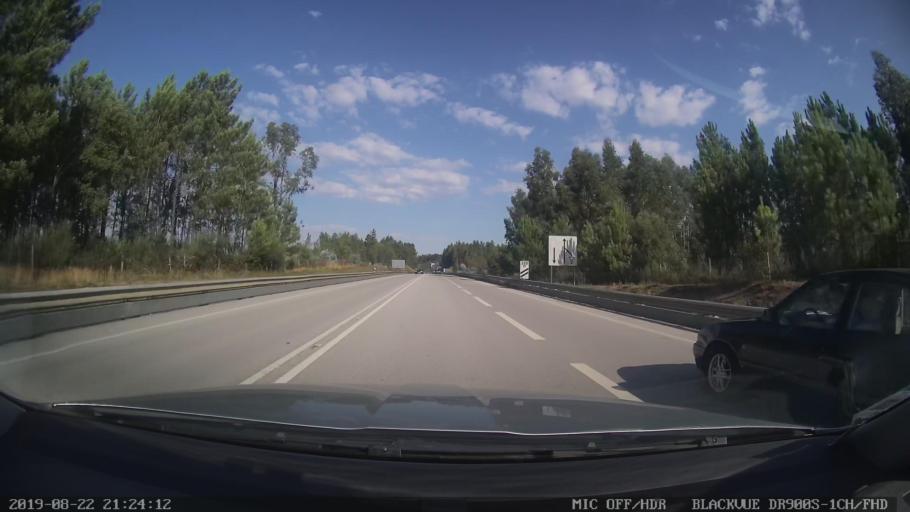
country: PT
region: Castelo Branco
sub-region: Serta
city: Serta
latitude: 39.8389
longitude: -8.1188
